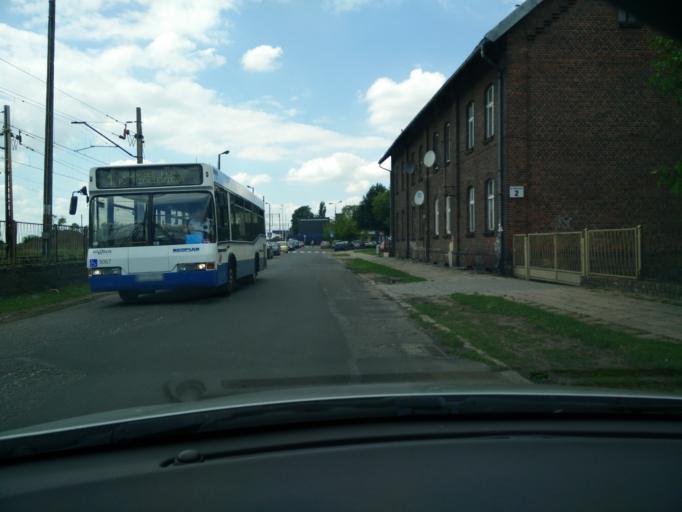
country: PL
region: Greater Poland Voivodeship
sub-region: Powiat sredzki
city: Sroda Wielkopolska
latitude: 52.2171
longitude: 17.2772
